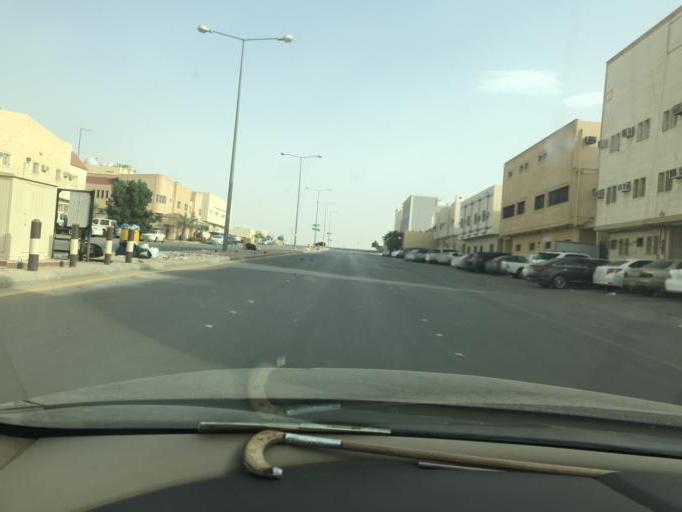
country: SA
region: Ar Riyad
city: Riyadh
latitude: 24.7827
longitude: 46.7150
